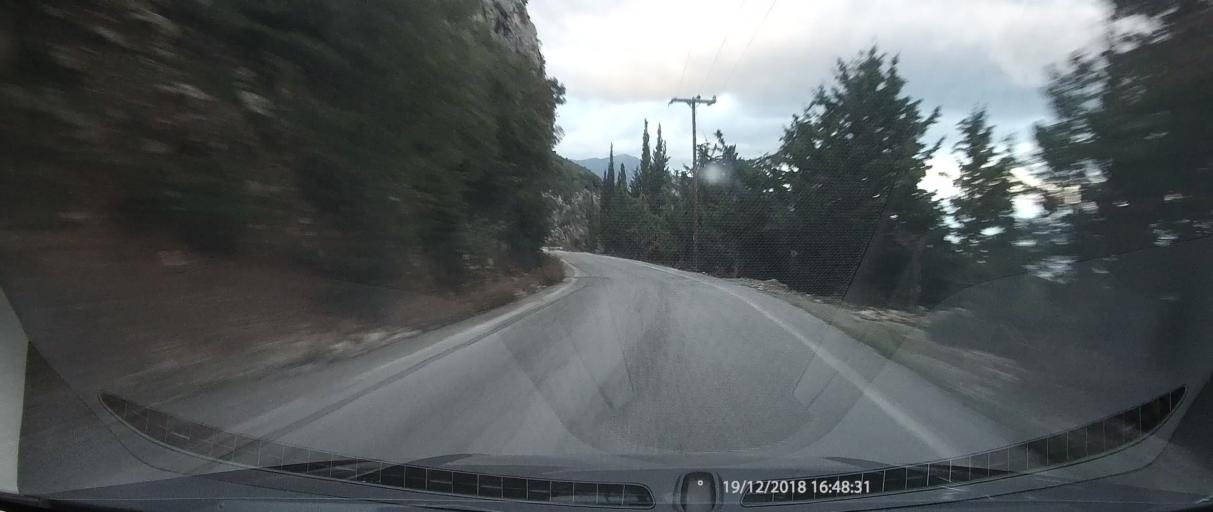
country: GR
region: Peloponnese
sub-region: Nomos Lakonias
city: Sykea
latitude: 36.9375
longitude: 22.9981
